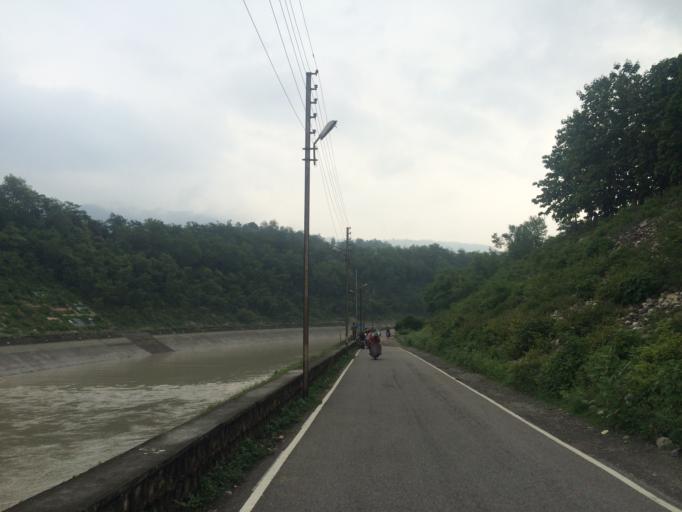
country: IN
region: Uttarakhand
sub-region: Dehradun
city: Birbhaddar
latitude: 30.0732
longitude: 78.2907
